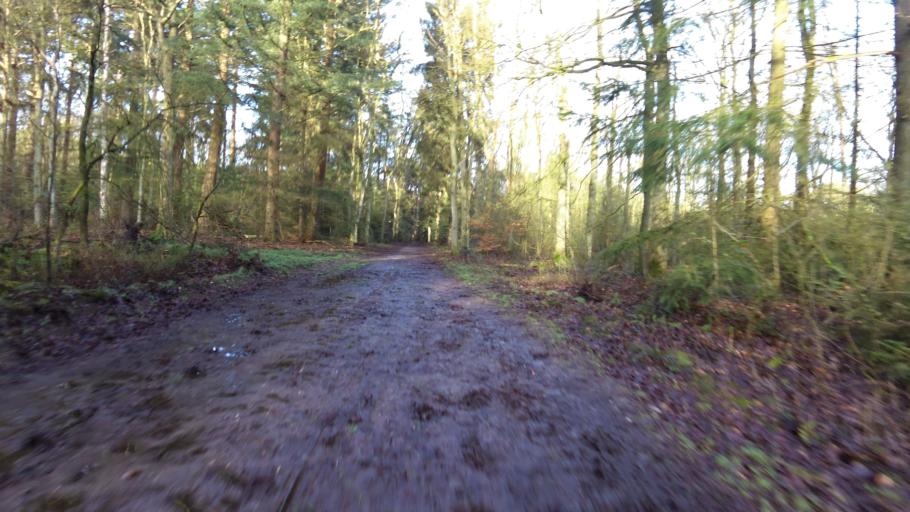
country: NL
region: Gelderland
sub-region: Gemeente Epe
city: Vaassen
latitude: 52.2634
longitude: 5.9330
